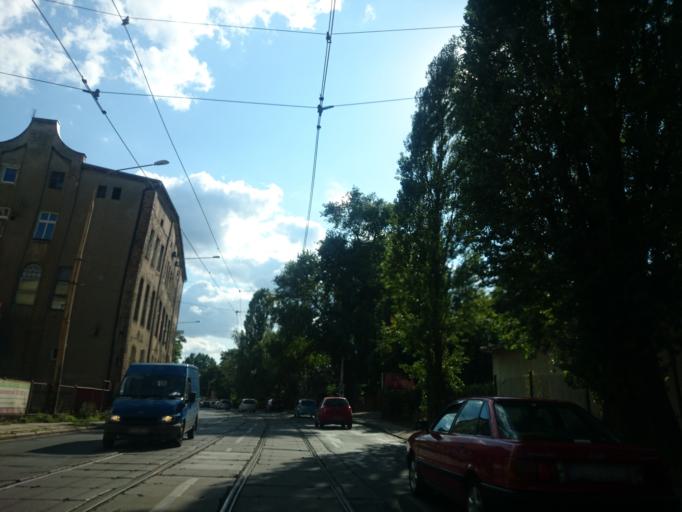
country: PL
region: West Pomeranian Voivodeship
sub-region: Szczecin
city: Szczecin
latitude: 53.4139
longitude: 14.5455
